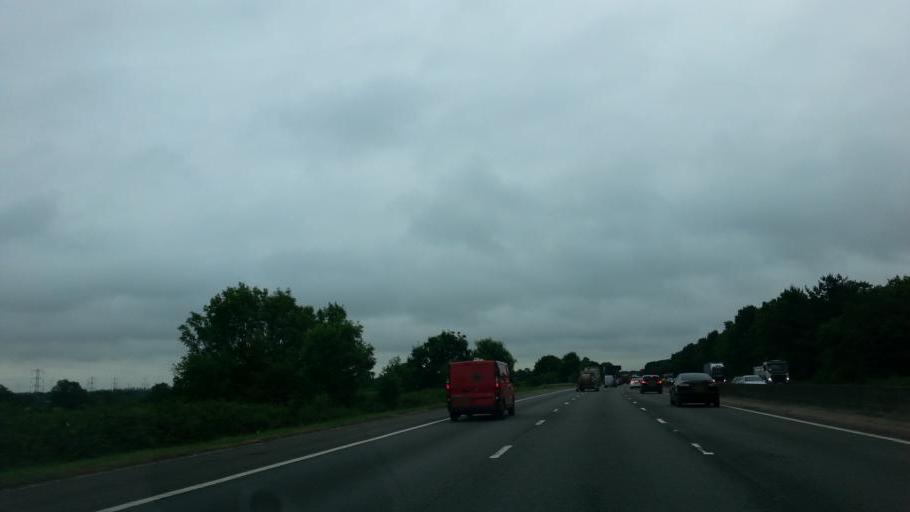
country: GB
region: England
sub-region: Leicestershire
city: Lutterworth
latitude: 52.4694
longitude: -1.1924
